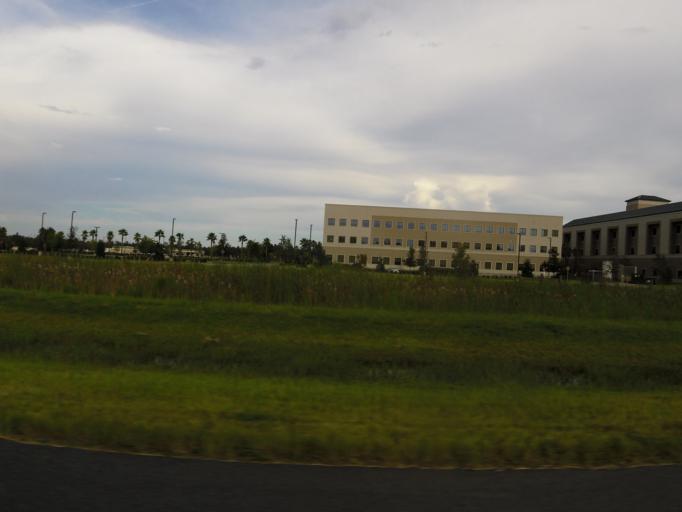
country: US
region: Florida
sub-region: Clay County
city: Middleburg
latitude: 30.1104
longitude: -81.8339
